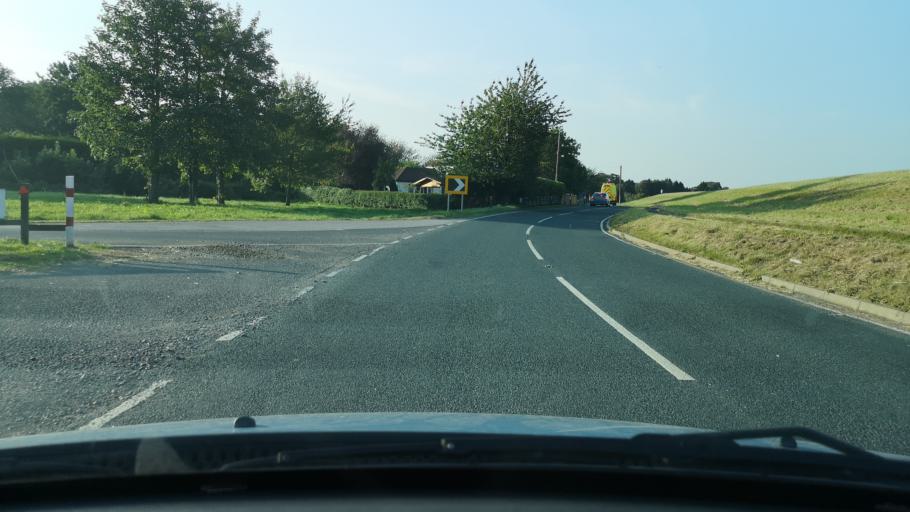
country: GB
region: England
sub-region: East Riding of Yorkshire
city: Goole
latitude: 53.6846
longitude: -0.8586
